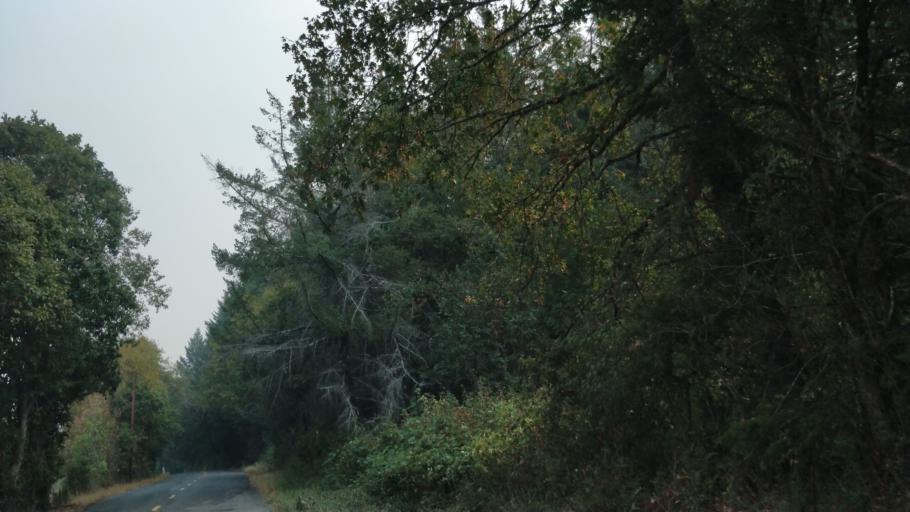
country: US
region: California
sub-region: Humboldt County
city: Rio Dell
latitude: 40.2387
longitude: -124.1618
